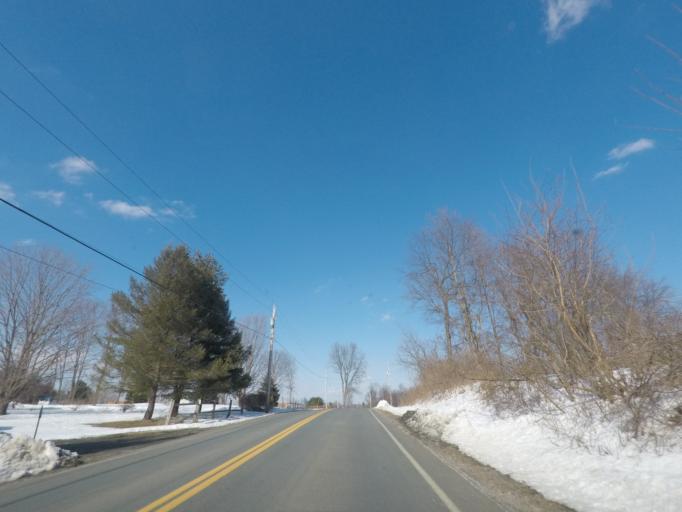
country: US
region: New York
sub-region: Saratoga County
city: Stillwater
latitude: 42.8552
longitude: -73.5999
